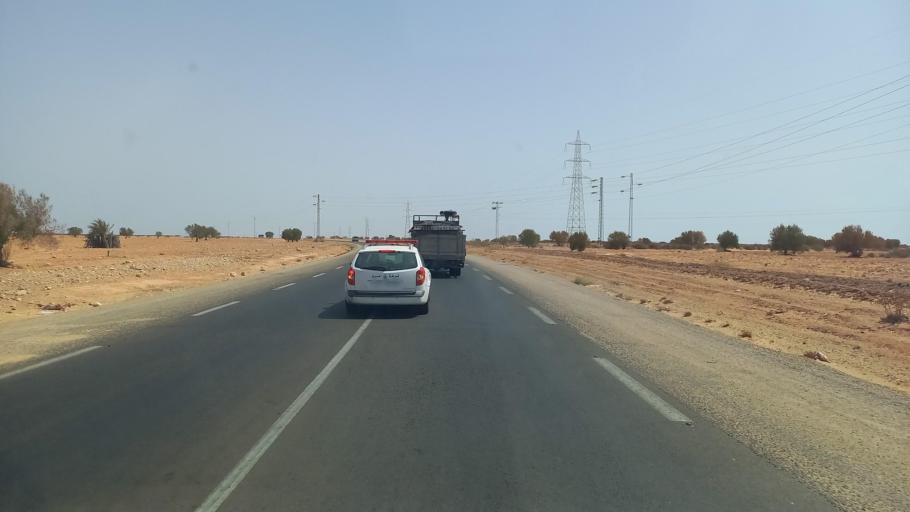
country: TN
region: Madanin
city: Zarzis
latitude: 33.4047
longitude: 10.8552
